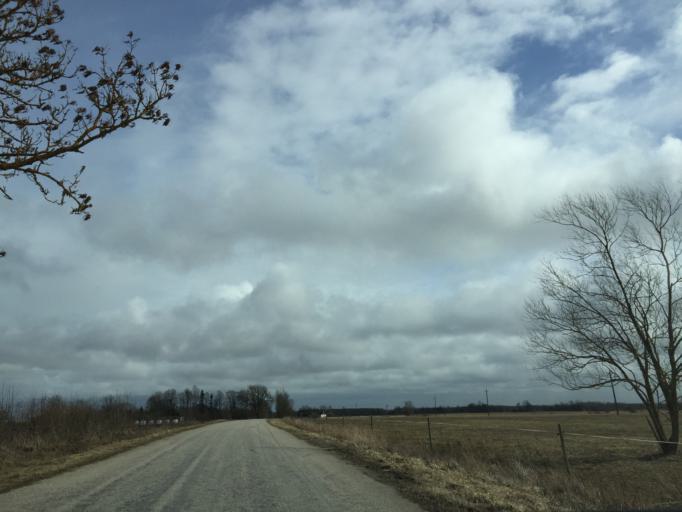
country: EE
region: Laeaene
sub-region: Lihula vald
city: Lihula
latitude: 58.7356
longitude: 23.8409
